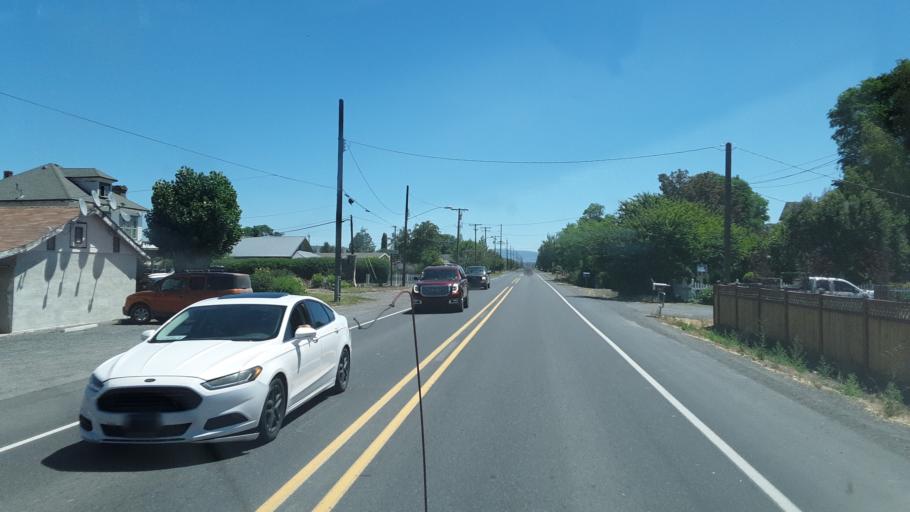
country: US
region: California
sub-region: Siskiyou County
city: Tulelake
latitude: 42.0239
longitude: -121.5938
